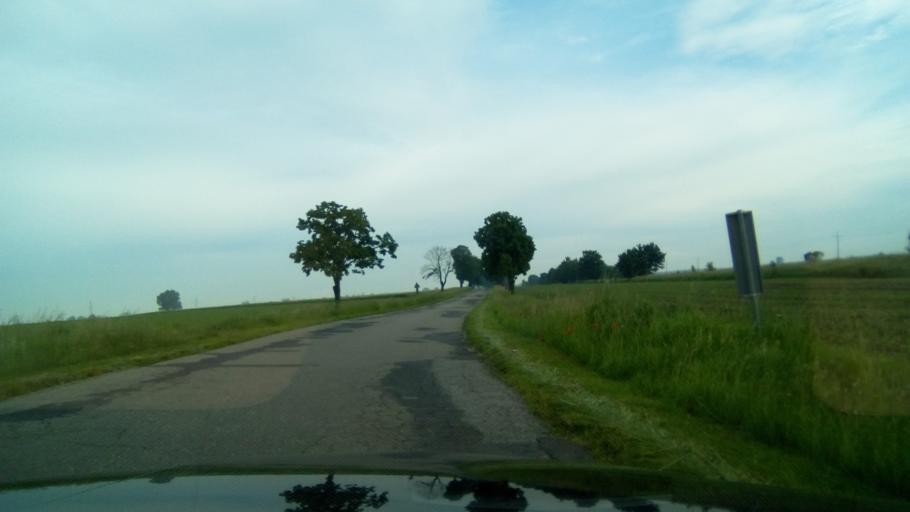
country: PL
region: Greater Poland Voivodeship
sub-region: Powiat gnieznienski
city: Mieleszyn
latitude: 52.6210
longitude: 17.5328
